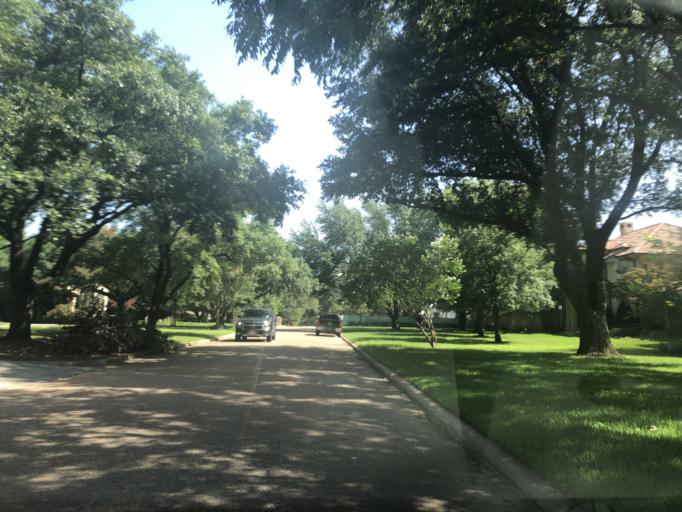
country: US
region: Texas
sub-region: Dallas County
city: University Park
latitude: 32.8826
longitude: -96.8190
